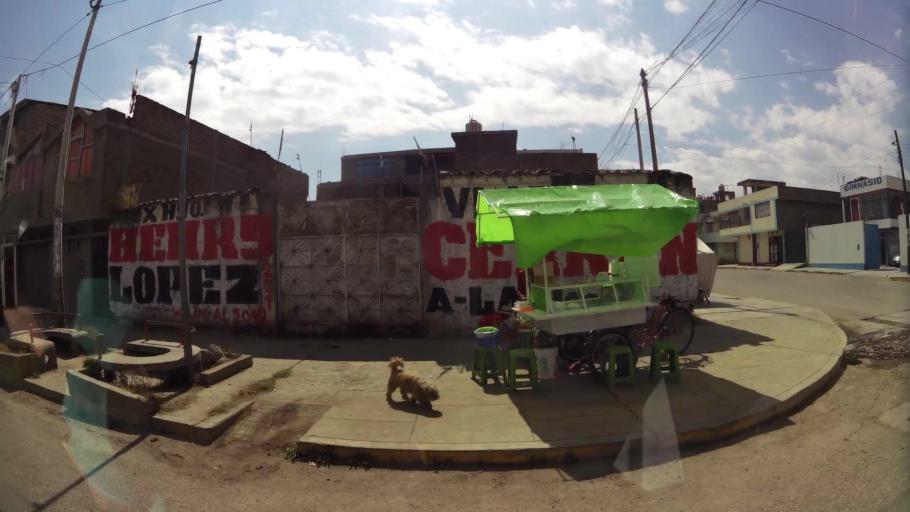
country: PE
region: Junin
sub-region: Provincia de Huancayo
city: Huancayo
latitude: -12.0755
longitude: -75.1961
